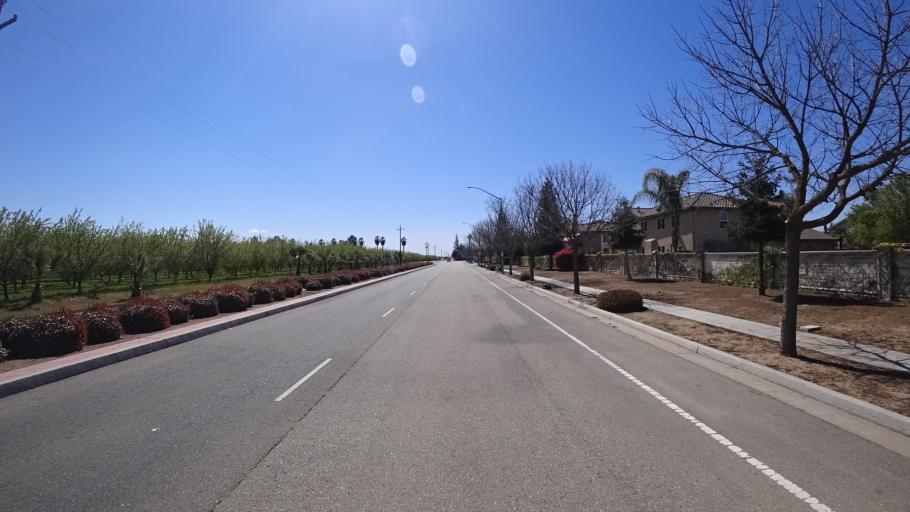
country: US
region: California
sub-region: Fresno County
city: West Park
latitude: 36.7308
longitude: -119.8446
